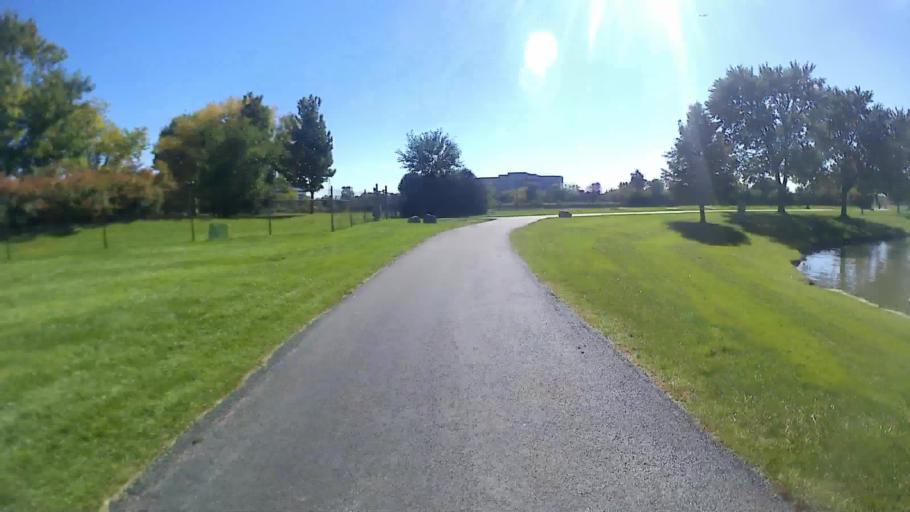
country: US
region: Illinois
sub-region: DuPage County
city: Itasca
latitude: 41.9901
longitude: -88.0086
